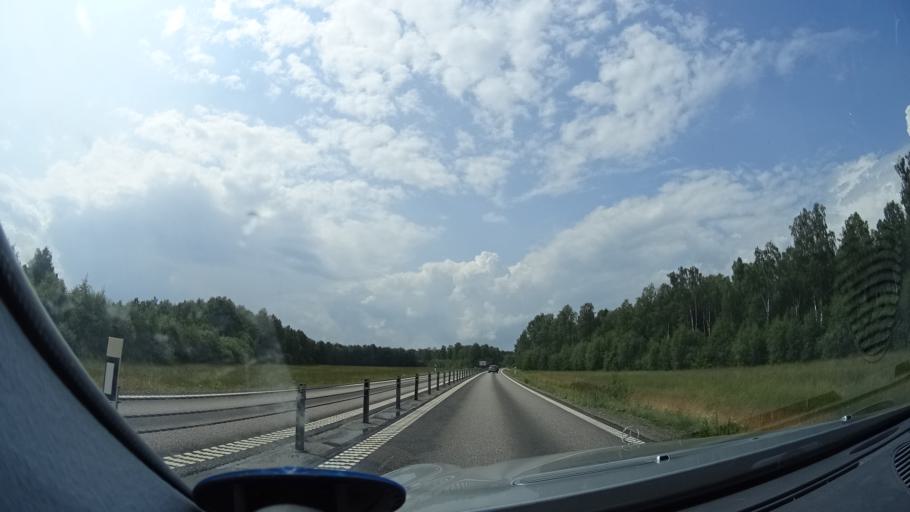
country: SE
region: Kalmar
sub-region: Nybro Kommun
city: Nybro
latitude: 56.7340
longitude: 15.8668
